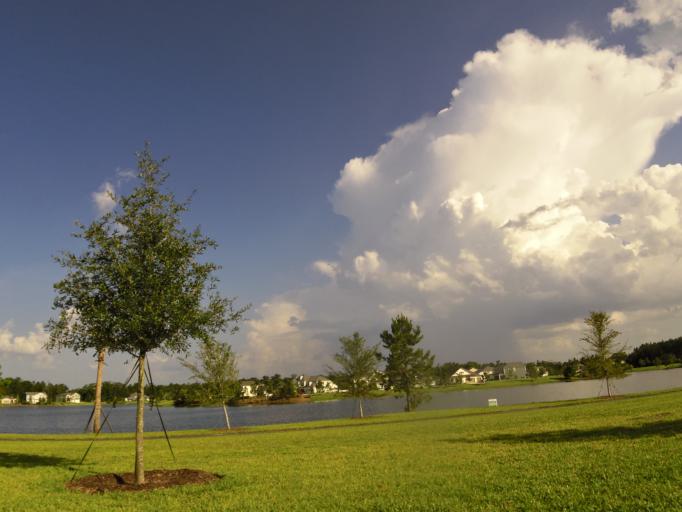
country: US
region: Florida
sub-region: Clay County
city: Green Cove Springs
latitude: 30.0303
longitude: -81.6340
